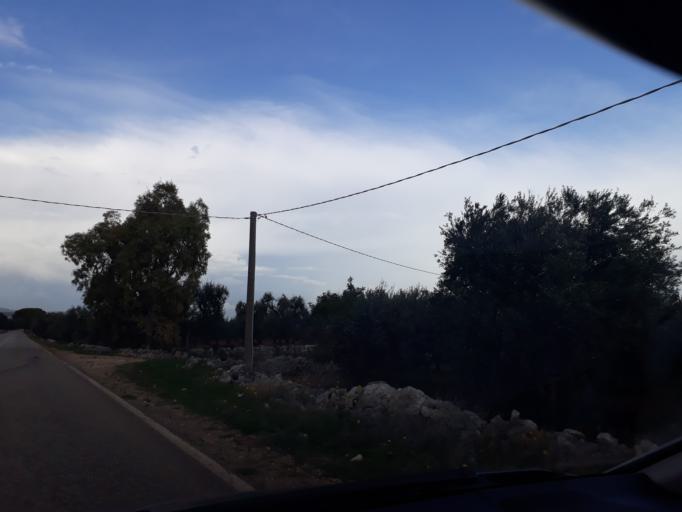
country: IT
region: Apulia
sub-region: Provincia di Brindisi
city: Pezze di Greco
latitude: 40.8043
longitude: 17.3938
